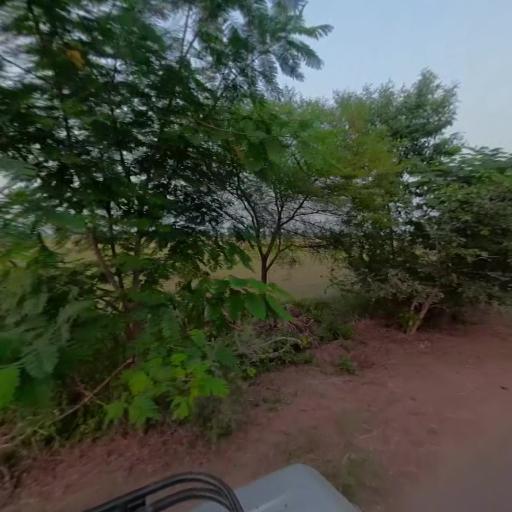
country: IN
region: Telangana
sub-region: Nalgonda
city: Suriapet
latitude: 17.0771
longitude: 79.5492
